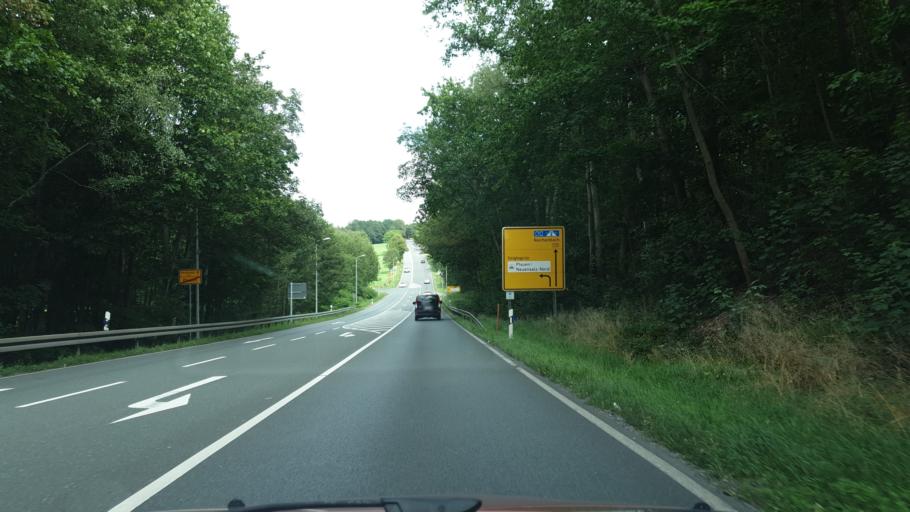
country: DE
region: Saxony
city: Neuensalz
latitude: 50.4972
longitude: 12.1800
